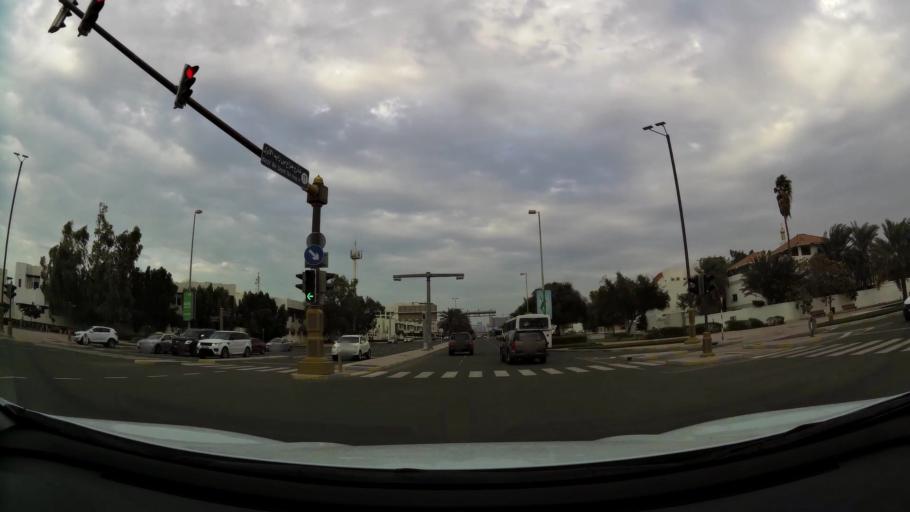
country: AE
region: Abu Dhabi
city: Abu Dhabi
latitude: 24.4539
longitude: 54.3526
